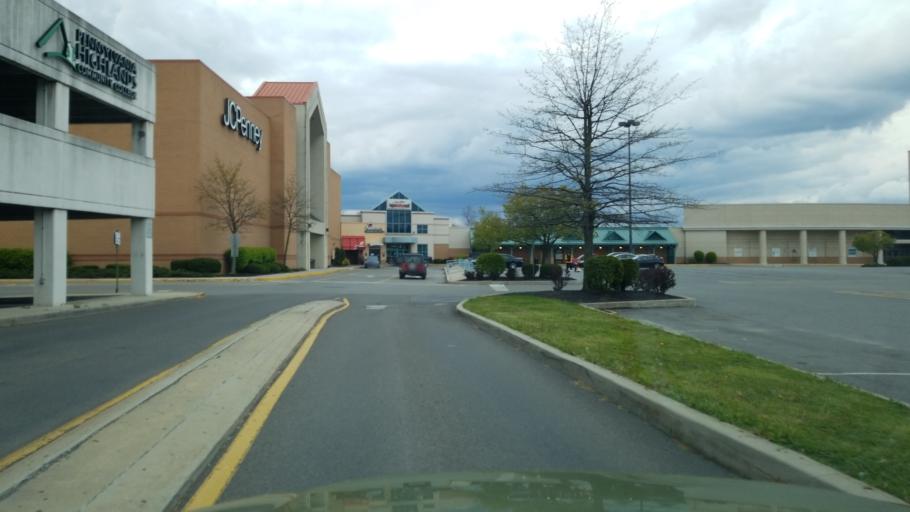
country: US
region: Pennsylvania
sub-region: Blair County
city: Lakemont
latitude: 40.4683
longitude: -78.4096
